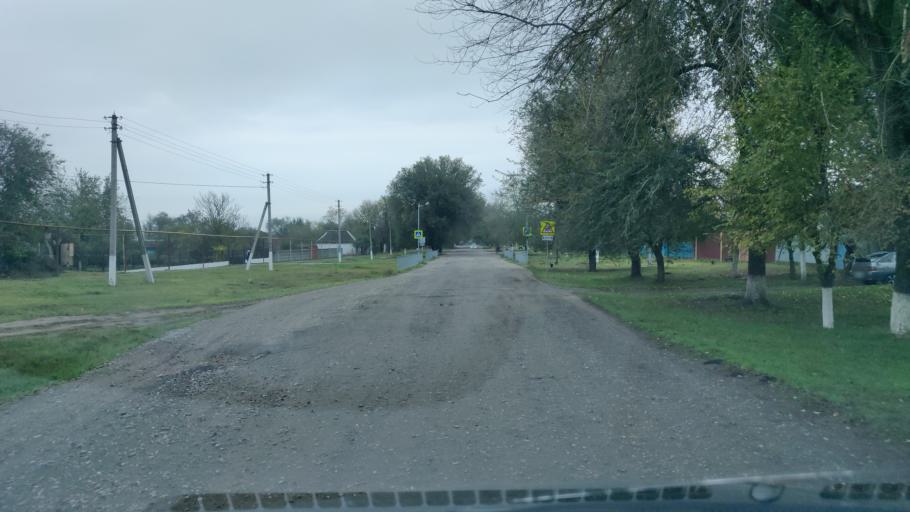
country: RU
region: Stavropol'skiy
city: Irgakly
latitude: 44.2449
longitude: 44.7198
